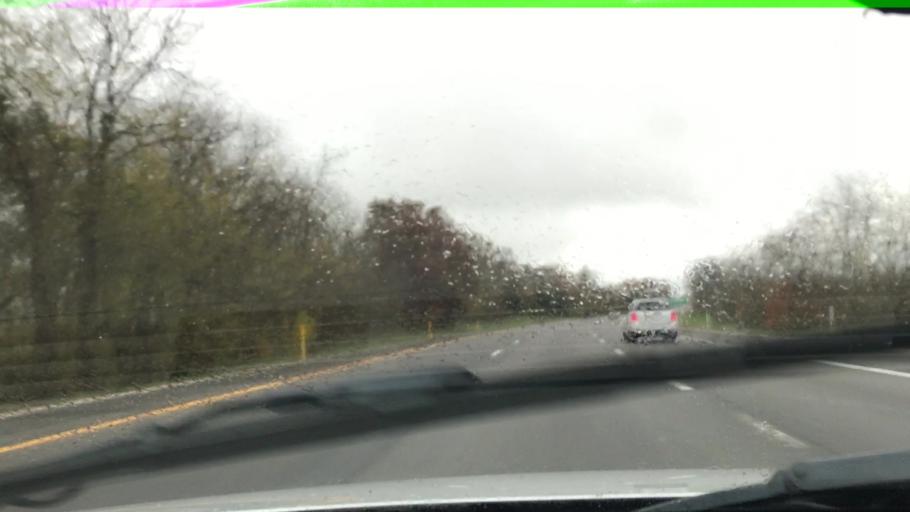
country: US
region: Kentucky
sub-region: Warren County
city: Bowling Green
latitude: 37.0130
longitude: -86.2916
